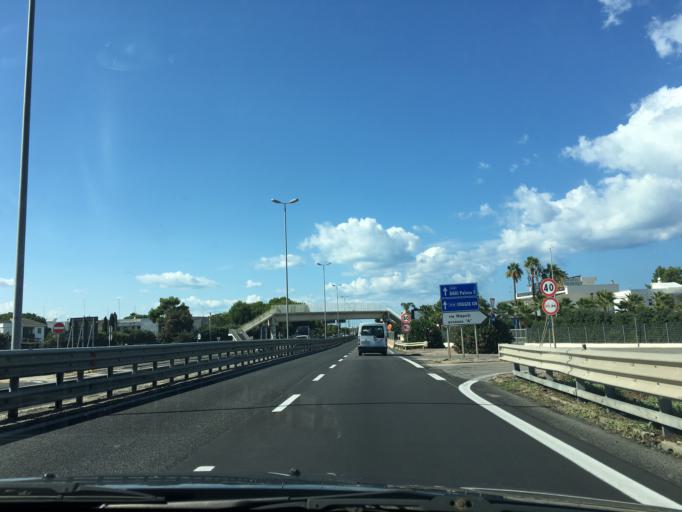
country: IT
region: Apulia
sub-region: Provincia di Bari
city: San Paolo
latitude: 41.1396
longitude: 16.8044
